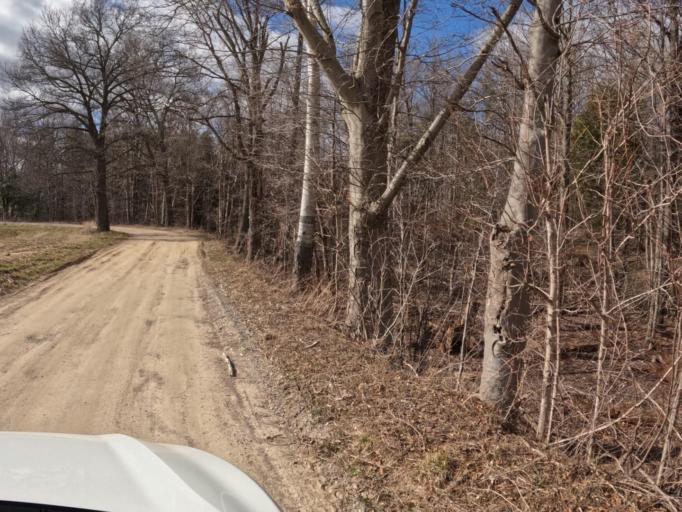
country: CA
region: Ontario
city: Norfolk County
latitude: 42.7654
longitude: -80.2967
